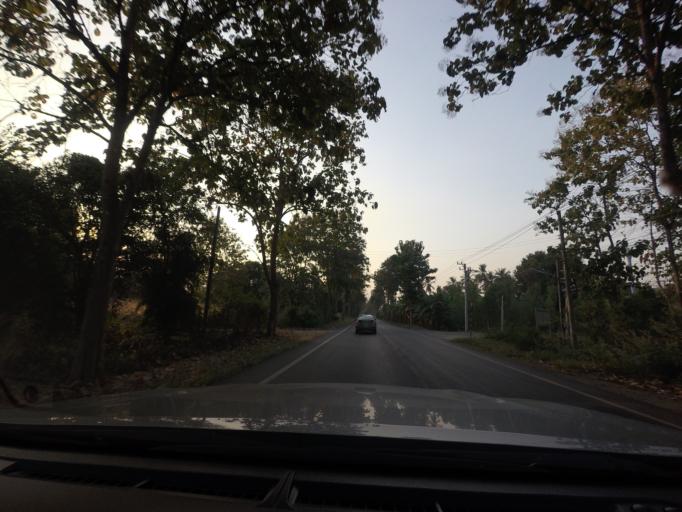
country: TH
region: Phitsanulok
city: Wang Thong
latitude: 16.7359
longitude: 100.4493
